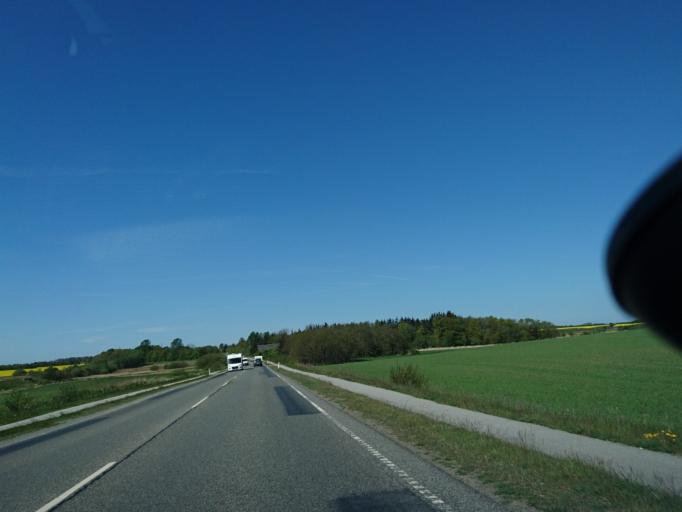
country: DK
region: North Denmark
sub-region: Hjorring Kommune
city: Tars
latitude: 57.4564
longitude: 10.0827
